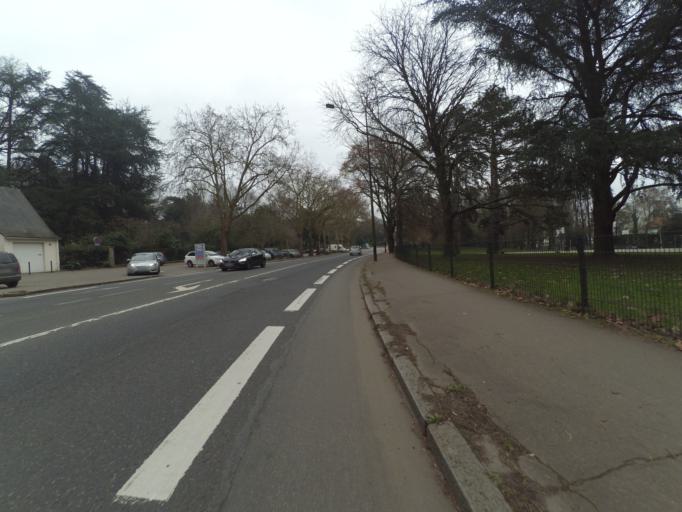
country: FR
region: Pays de la Loire
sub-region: Departement de la Loire-Atlantique
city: Nantes
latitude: 47.2225
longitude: -1.5806
